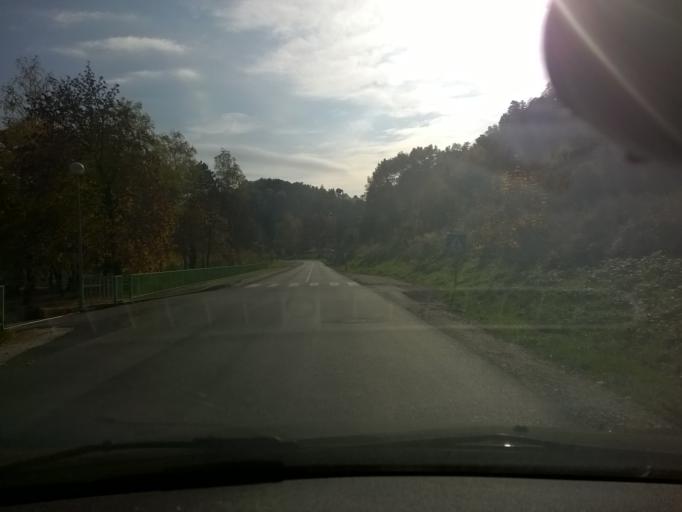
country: HR
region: Krapinsko-Zagorska
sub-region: Grad Krapina
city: Krapina
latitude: 46.1681
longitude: 15.8624
